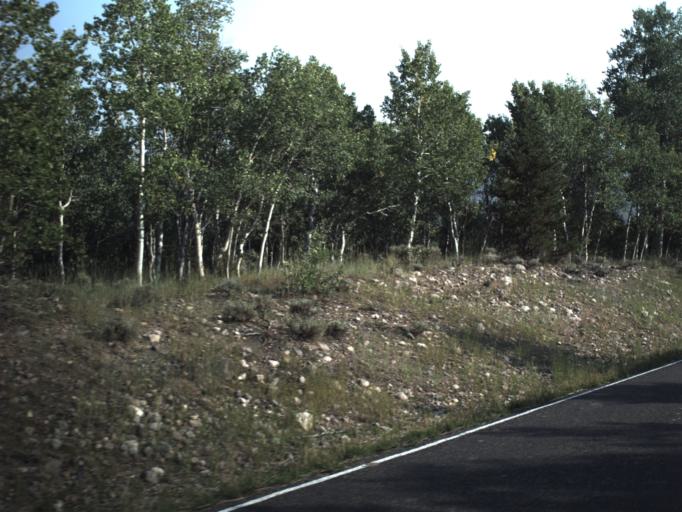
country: US
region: Wyoming
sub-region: Uinta County
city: Evanston
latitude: 40.8496
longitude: -110.8469
